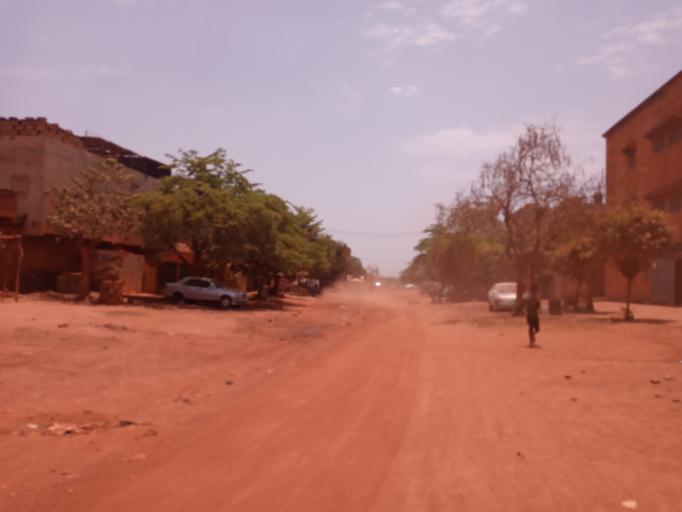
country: ML
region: Bamako
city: Bamako
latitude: 12.5578
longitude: -7.9823
